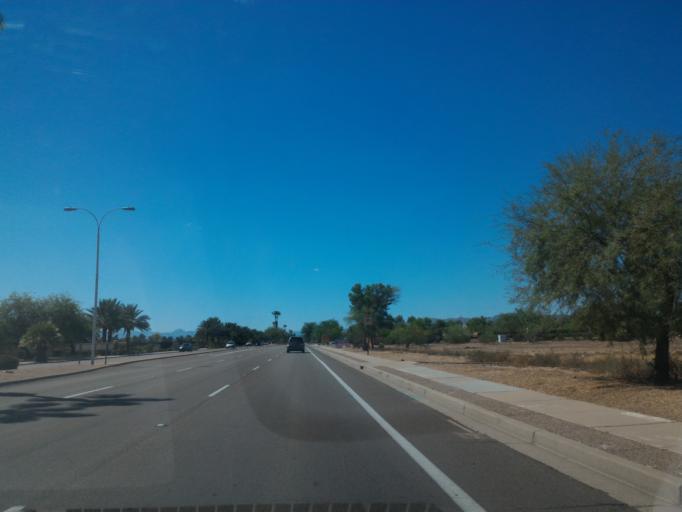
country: US
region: Arizona
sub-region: Maricopa County
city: Chandler
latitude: 33.3055
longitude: -111.9141
